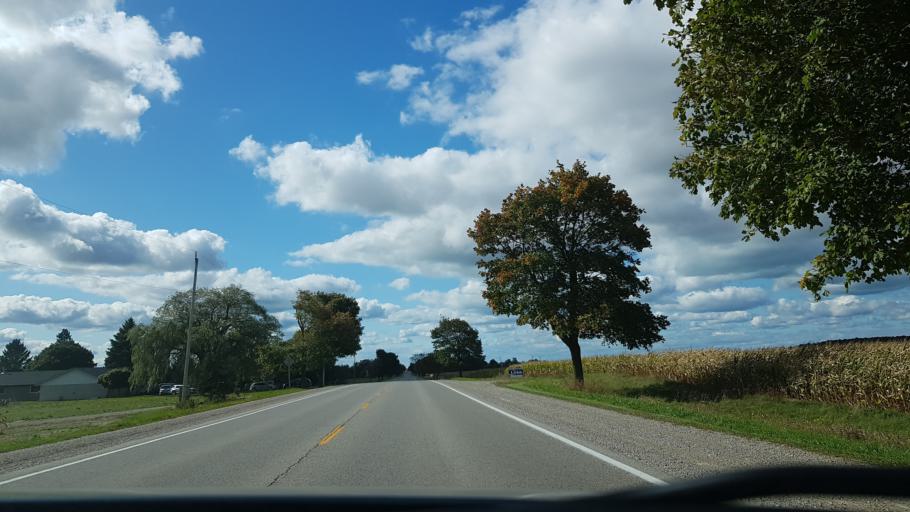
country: CA
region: Ontario
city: South Huron
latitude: 43.3484
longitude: -81.6120
